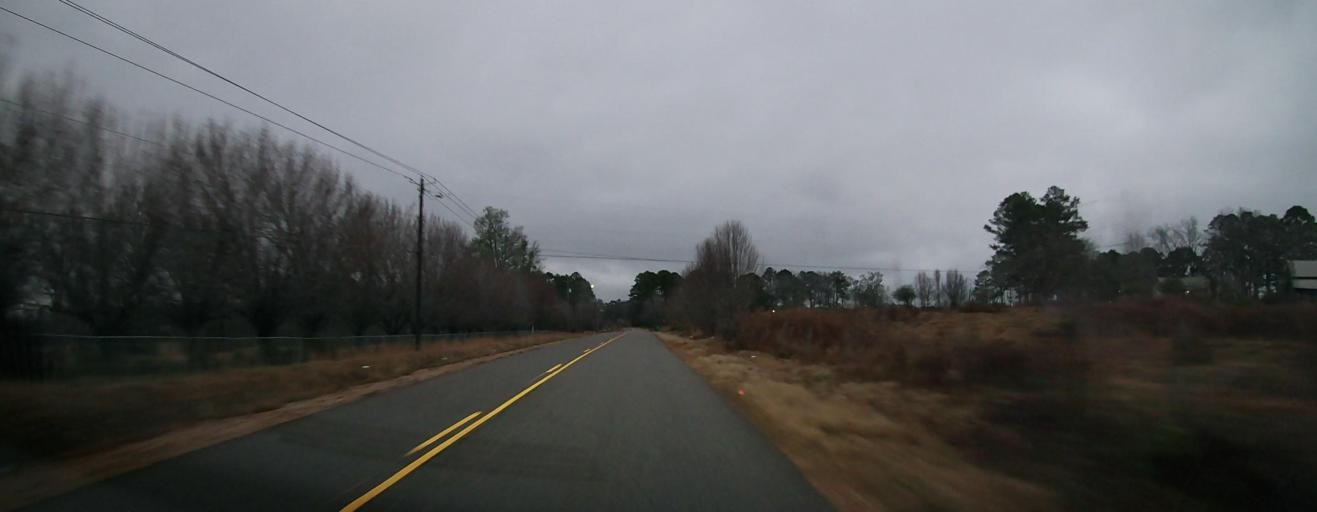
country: US
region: Alabama
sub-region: Tuscaloosa County
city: Vance
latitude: 33.1570
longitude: -87.2299
